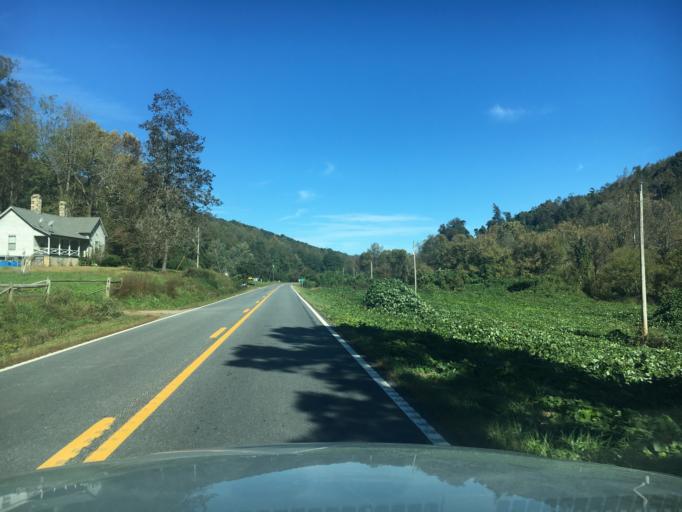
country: US
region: North Carolina
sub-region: Rutherford County
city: Spindale
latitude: 35.5396
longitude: -81.8565
